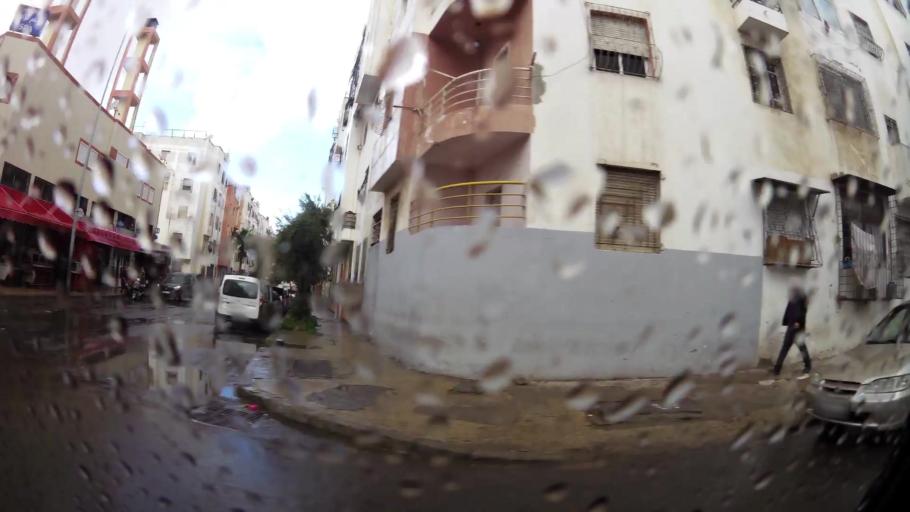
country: MA
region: Grand Casablanca
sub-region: Casablanca
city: Casablanca
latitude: 33.5454
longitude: -7.6748
